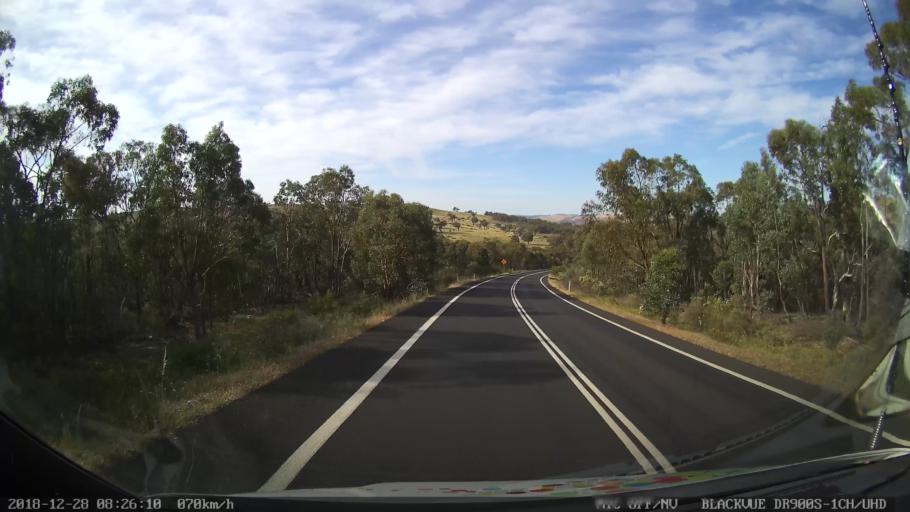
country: AU
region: New South Wales
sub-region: Blayney
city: Blayney
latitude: -33.9333
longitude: 149.3499
